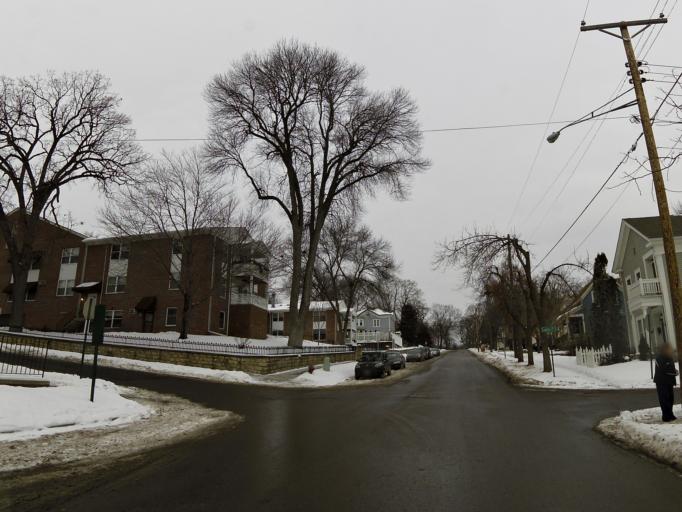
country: US
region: Minnesota
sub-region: Washington County
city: Stillwater
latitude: 45.0587
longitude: -92.8100
